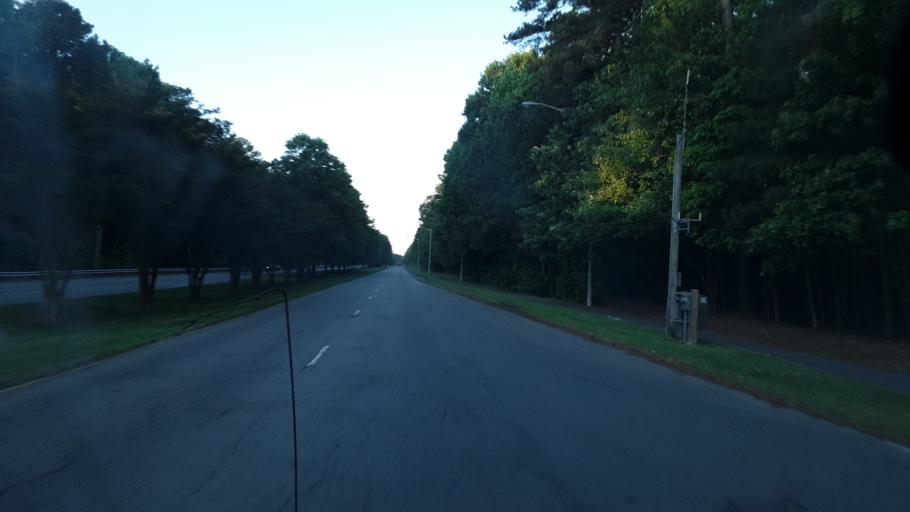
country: US
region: Virginia
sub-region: City of Virginia Beach
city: Virginia Beach
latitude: 36.8053
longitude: -75.9918
